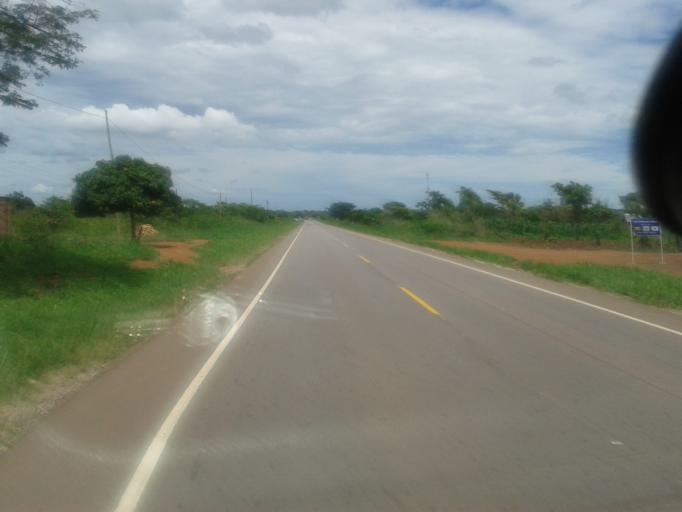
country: UG
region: Western Region
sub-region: Kiryandongo District
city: Masindi Port
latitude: 1.7181
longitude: 32.0273
